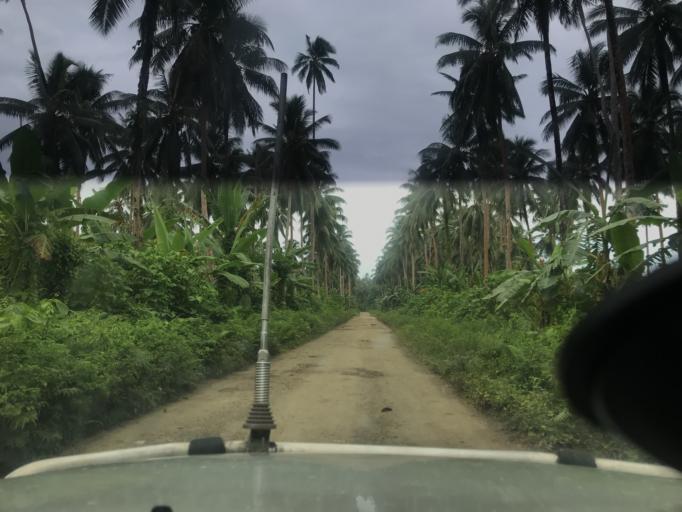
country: SB
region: Choiseul
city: Taro'a
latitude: -9.1273
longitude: 160.8446
